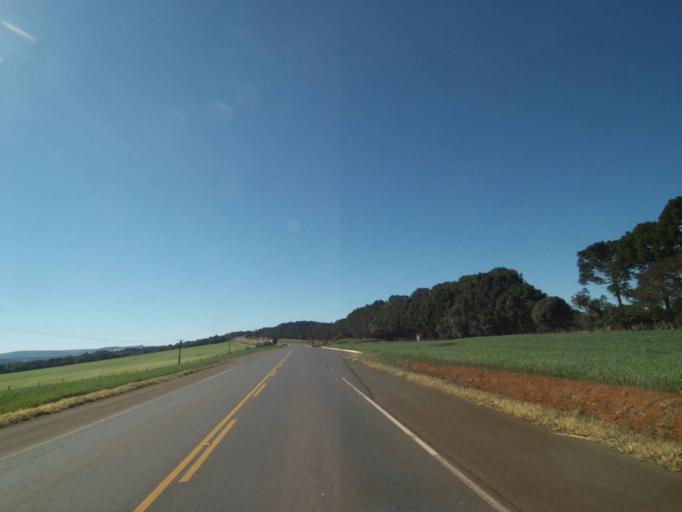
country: BR
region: Parana
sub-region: Tibagi
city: Tibagi
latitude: -24.4188
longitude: -50.3699
